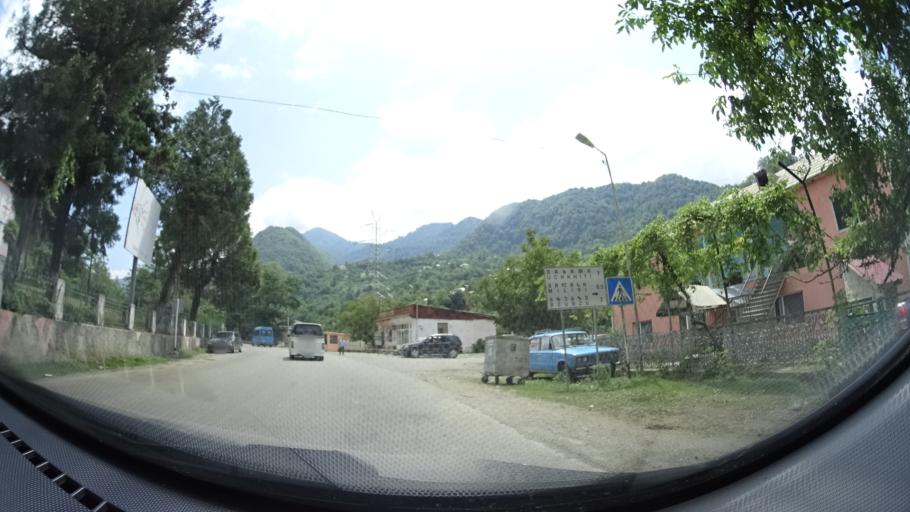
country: TR
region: Artvin
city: Camili
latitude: 41.5654
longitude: 41.8318
